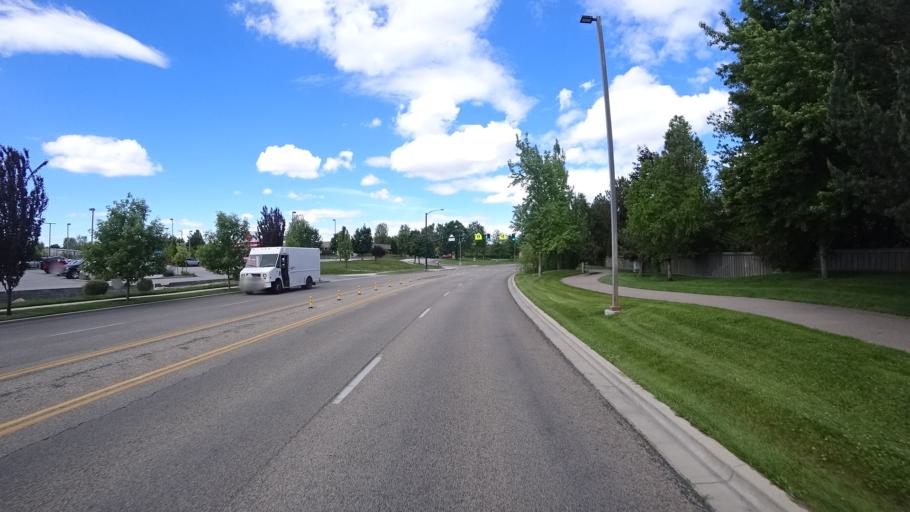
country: US
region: Idaho
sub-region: Ada County
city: Boise
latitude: 43.5755
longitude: -116.1552
